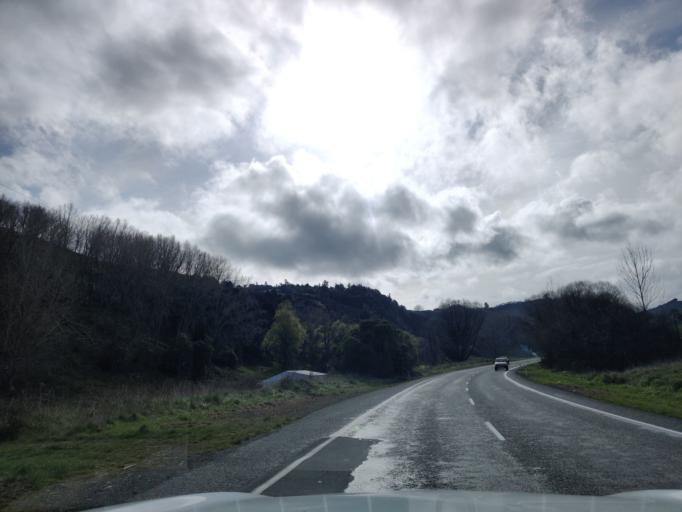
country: NZ
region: Manawatu-Wanganui
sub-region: Ruapehu District
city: Waiouru
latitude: -39.8411
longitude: 175.7423
